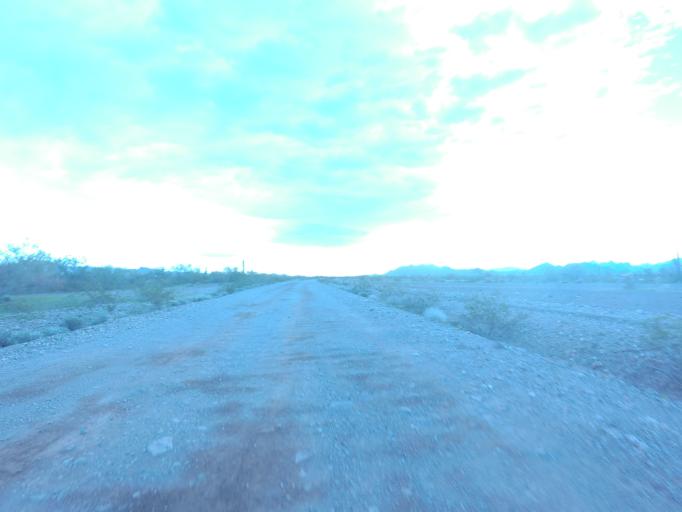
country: US
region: Arizona
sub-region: La Paz County
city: Quartzsite
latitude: 33.5349
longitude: -114.2029
